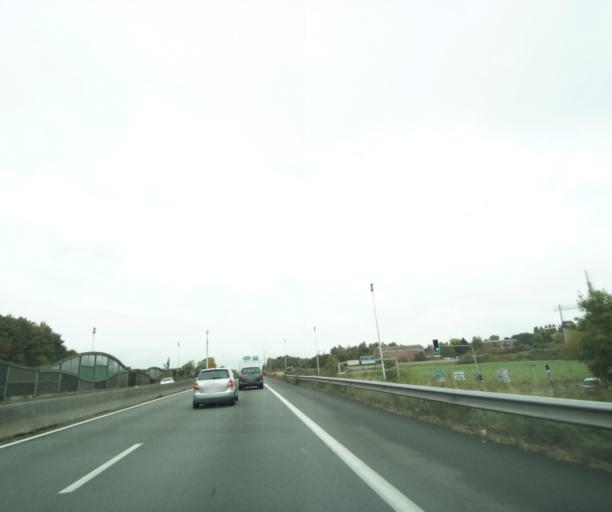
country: FR
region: Nord-Pas-de-Calais
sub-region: Departement du Nord
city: Mons-en-Baroeul
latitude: 50.6367
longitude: 3.1423
